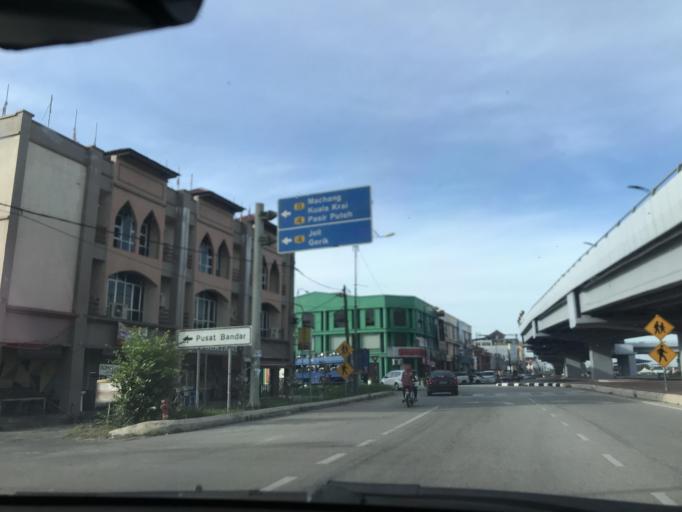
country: MY
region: Kelantan
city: Tanah Merah
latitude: 5.8109
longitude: 102.1478
